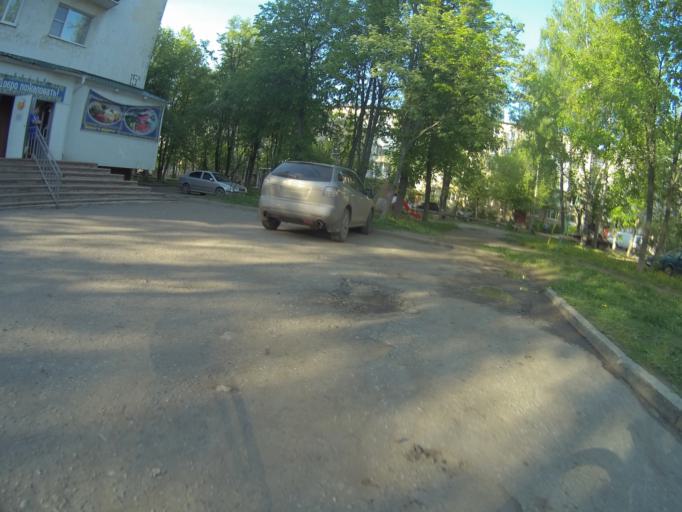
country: RU
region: Vladimir
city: Kommunar
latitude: 56.1681
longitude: 40.4619
